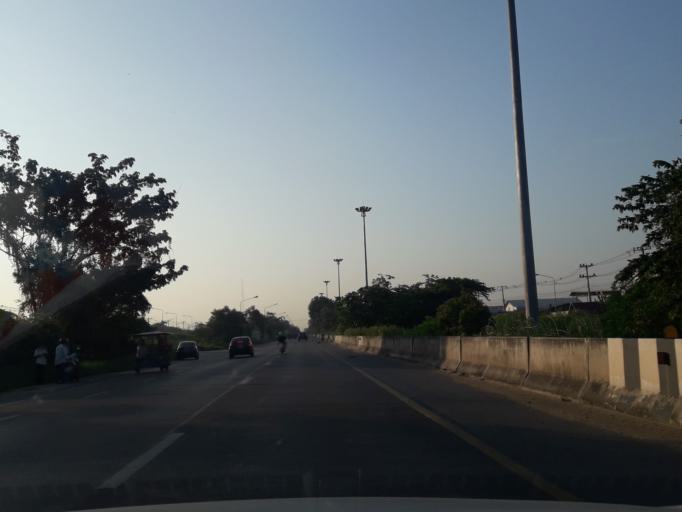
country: TH
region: Phra Nakhon Si Ayutthaya
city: Bang Pa-in
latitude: 14.1893
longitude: 100.5546
